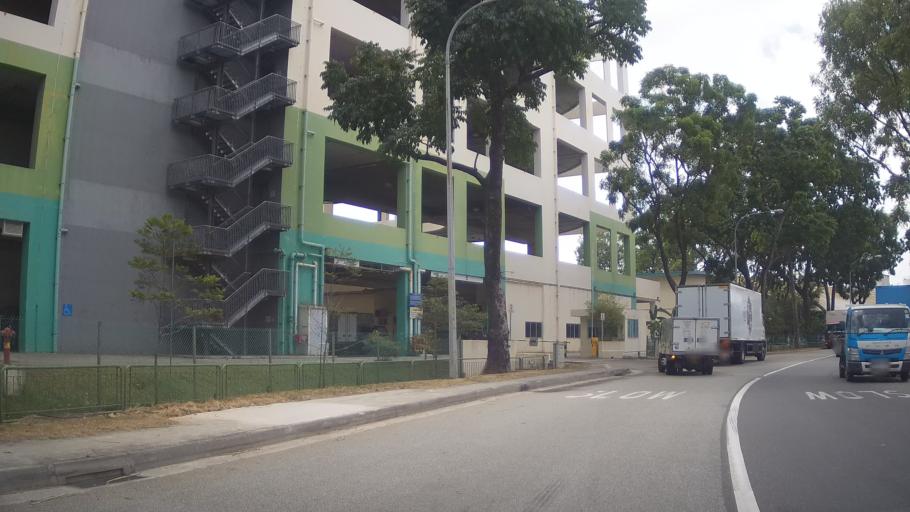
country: SG
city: Singapore
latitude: 1.3088
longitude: 103.7217
